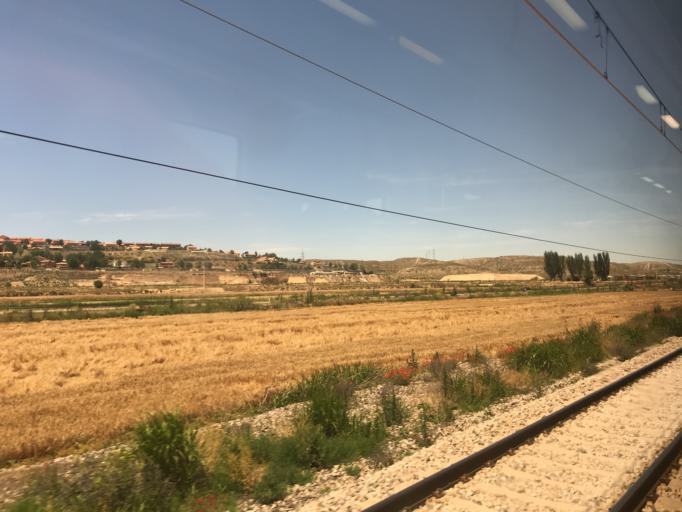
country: ES
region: Madrid
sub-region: Provincia de Madrid
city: Ciempozuelos
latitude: 40.1056
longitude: -3.6248
